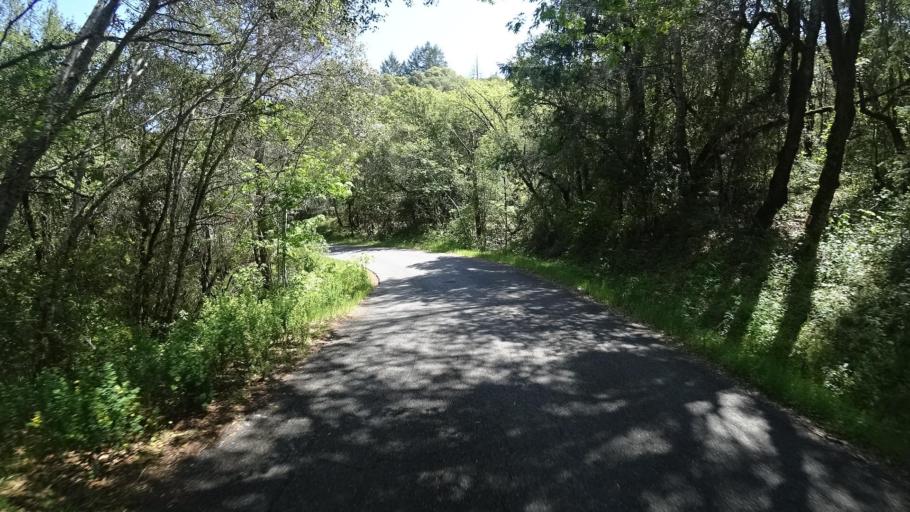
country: US
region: California
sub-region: Humboldt County
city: Redway
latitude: 40.1895
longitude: -123.5674
